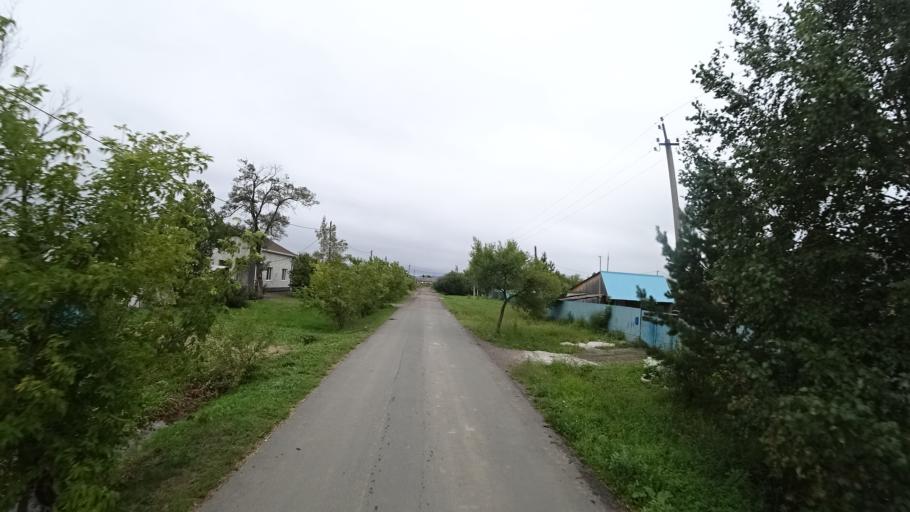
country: RU
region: Primorskiy
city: Chernigovka
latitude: 44.3272
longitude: 132.5991
